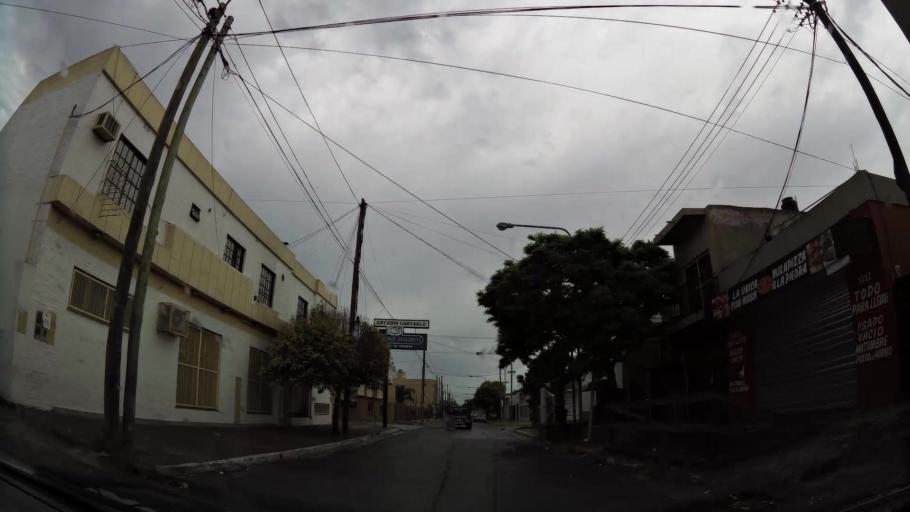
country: AR
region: Buenos Aires
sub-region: Partido de Quilmes
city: Quilmes
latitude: -34.7636
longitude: -58.2228
